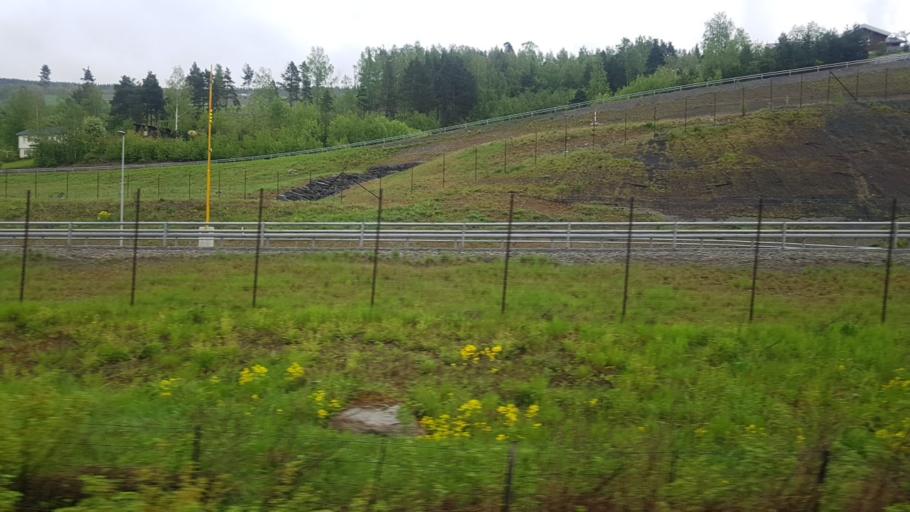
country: NO
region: Oppland
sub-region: Sor-Fron
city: Hundorp
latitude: 61.5556
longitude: 9.9446
